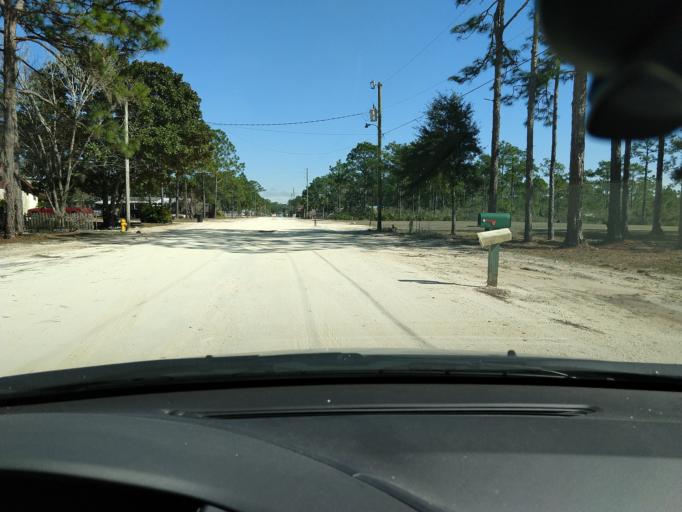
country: US
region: Florida
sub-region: Walton County
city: Miramar Beach
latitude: 30.3926
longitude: -86.3015
